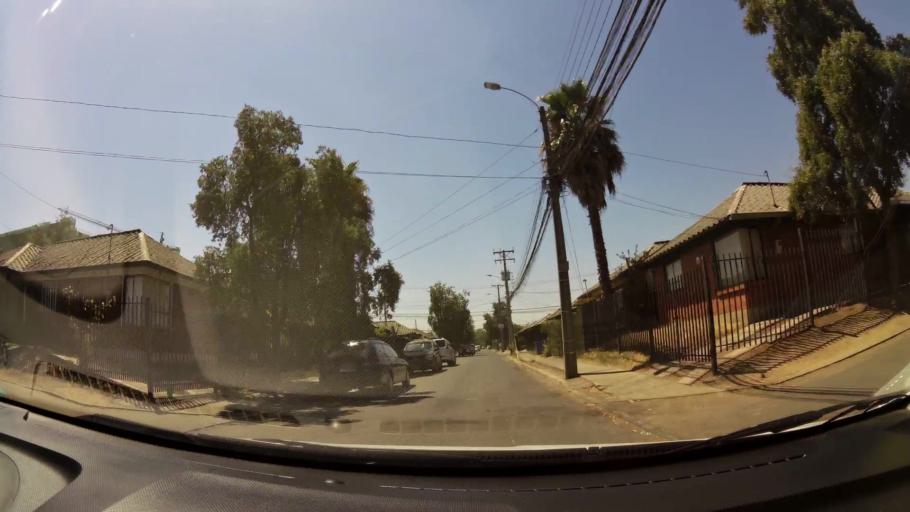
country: CL
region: Maule
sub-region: Provincia de Talca
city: Talca
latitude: -35.4306
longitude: -71.6257
